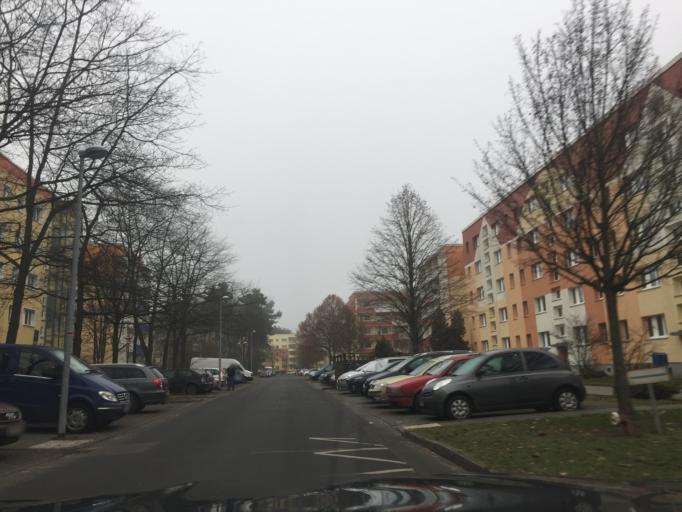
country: DE
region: Brandenburg
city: Hennigsdorf
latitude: 52.6542
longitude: 13.1972
